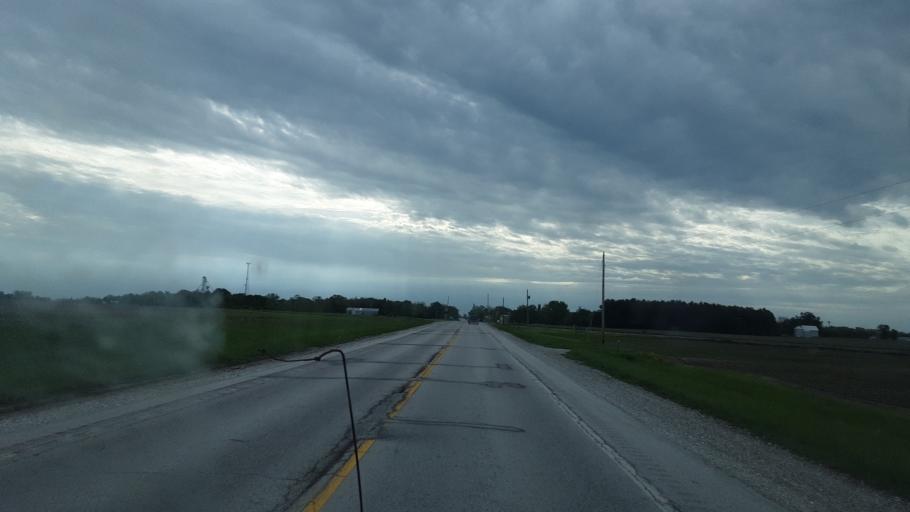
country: US
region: Illinois
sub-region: Hancock County
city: Hamilton
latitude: 40.3951
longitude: -91.2615
